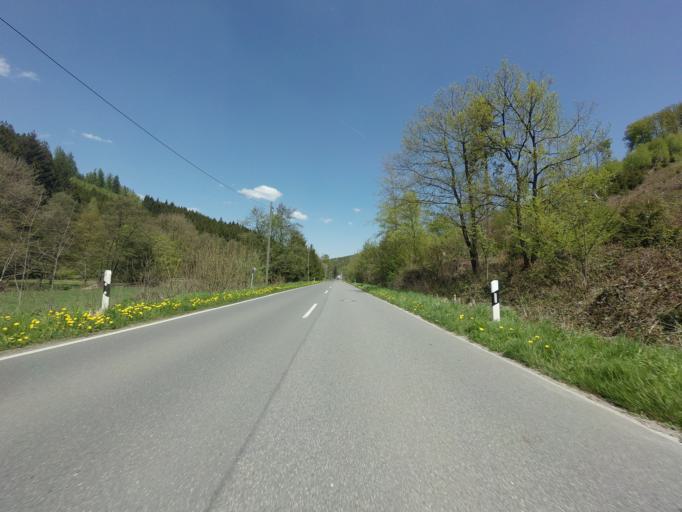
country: DE
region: North Rhine-Westphalia
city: Hemer
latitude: 51.3627
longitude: 7.7847
